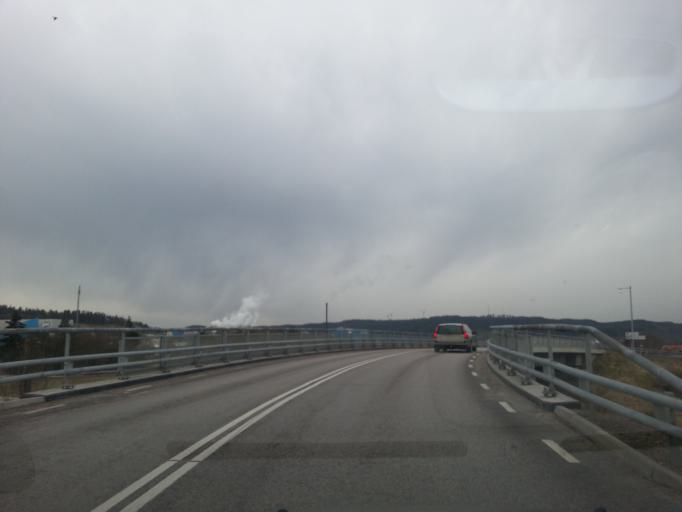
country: SE
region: Vaestra Goetaland
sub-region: Lilla Edets Kommun
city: Lilla Edet
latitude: 58.1248
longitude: 12.1381
